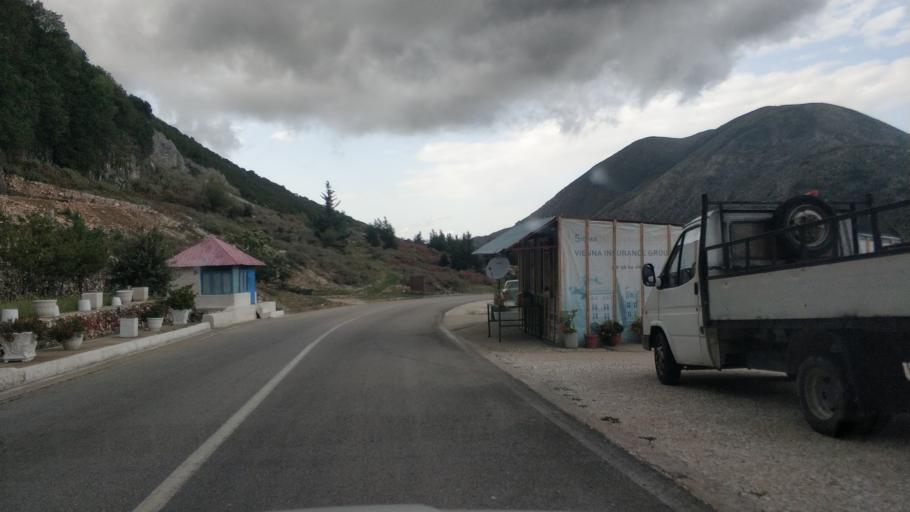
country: AL
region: Vlore
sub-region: Rrethi i Vlores
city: Orikum
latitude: 40.2380
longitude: 19.5520
